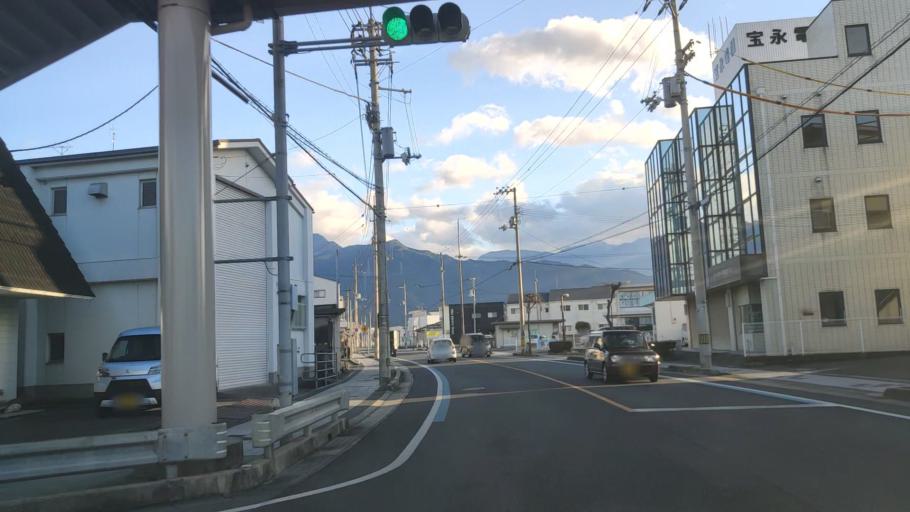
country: JP
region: Ehime
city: Saijo
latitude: 33.9146
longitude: 133.1780
